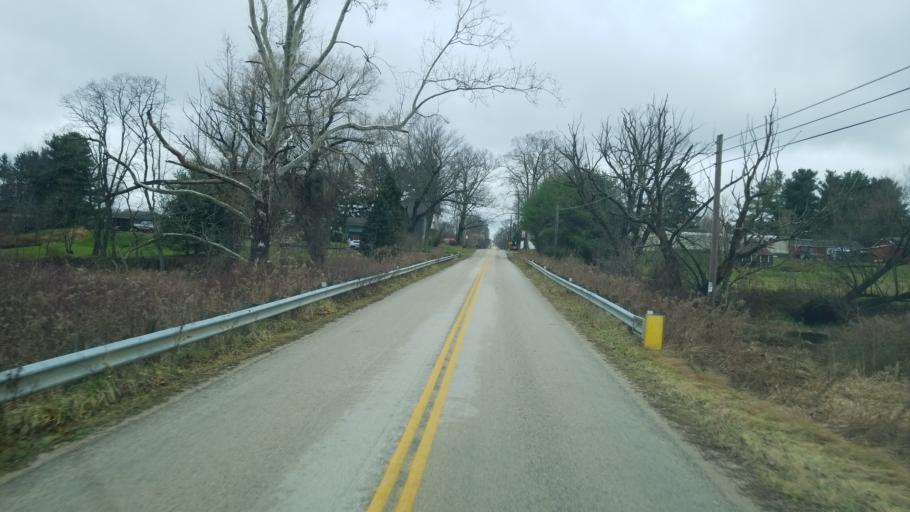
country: US
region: Ohio
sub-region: Ashtabula County
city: North Kingsville
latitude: 41.8543
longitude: -80.6174
